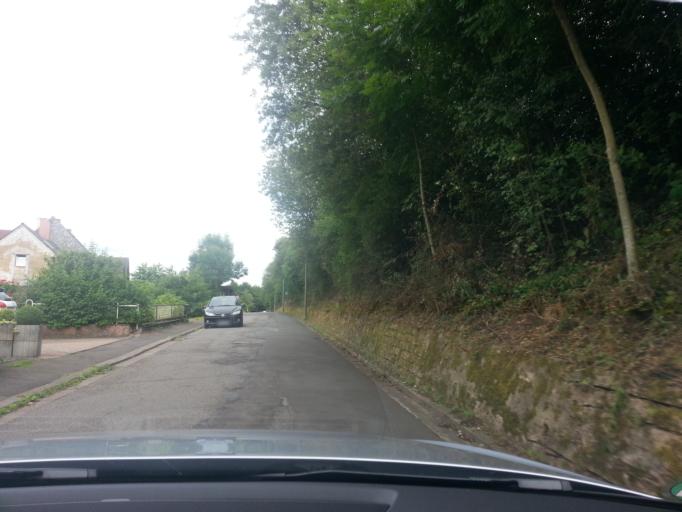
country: DE
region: Saarland
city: Schiffweiler
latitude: 49.3533
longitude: 7.1356
